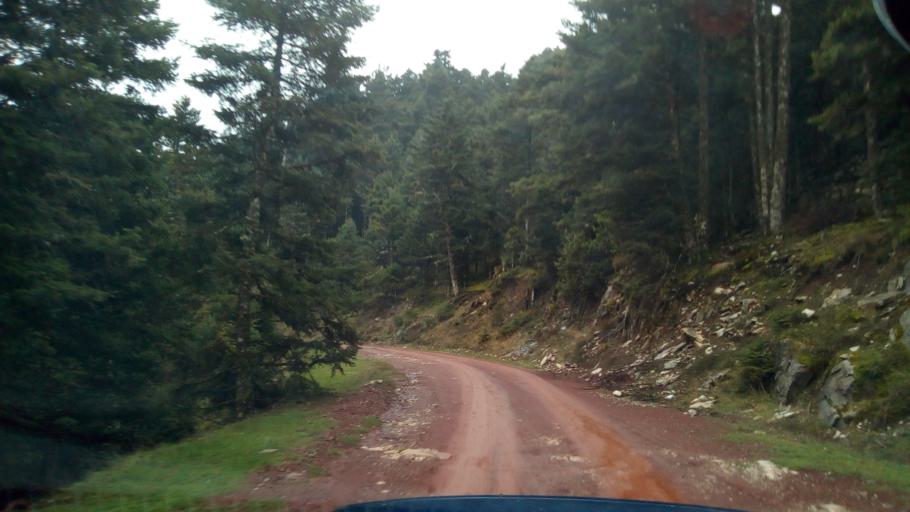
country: GR
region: West Greece
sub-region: Nomos Aitolias kai Akarnanias
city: Nafpaktos
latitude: 38.5387
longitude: 21.8588
